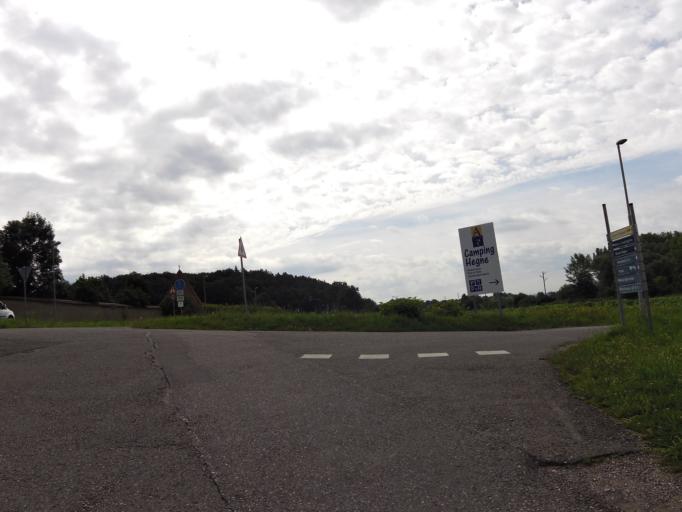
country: DE
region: Baden-Wuerttemberg
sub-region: Freiburg Region
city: Allensbach
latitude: 47.7070
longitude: 9.1003
